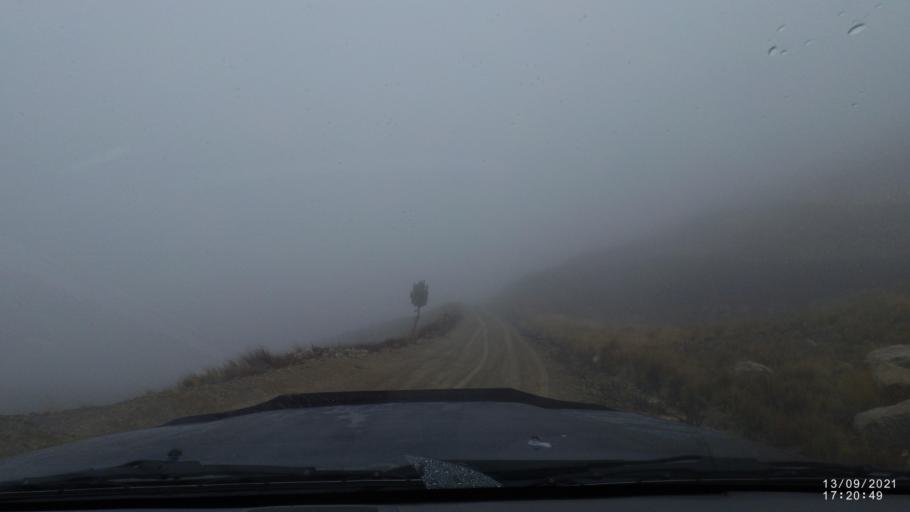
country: BO
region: Cochabamba
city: Colomi
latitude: -17.3530
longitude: -65.7673
